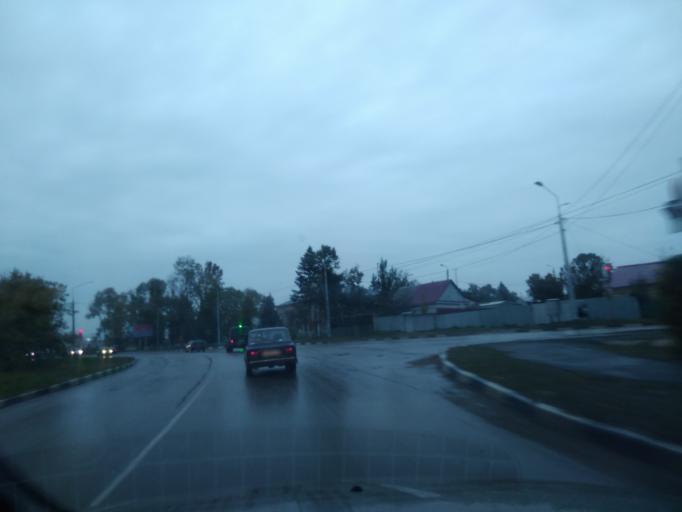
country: RU
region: Tula
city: Yefremov
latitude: 53.1454
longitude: 38.0993
